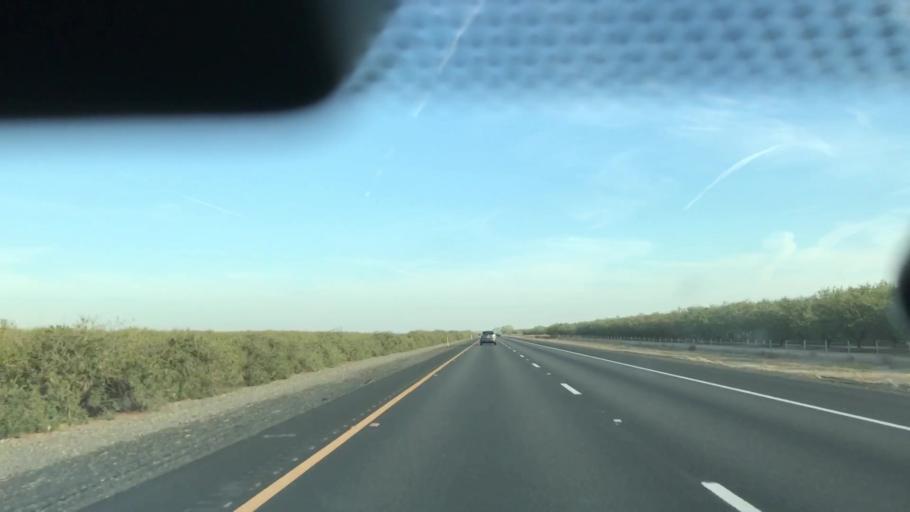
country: US
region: California
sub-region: Glenn County
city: Orland
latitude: 39.6496
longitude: -122.2042
